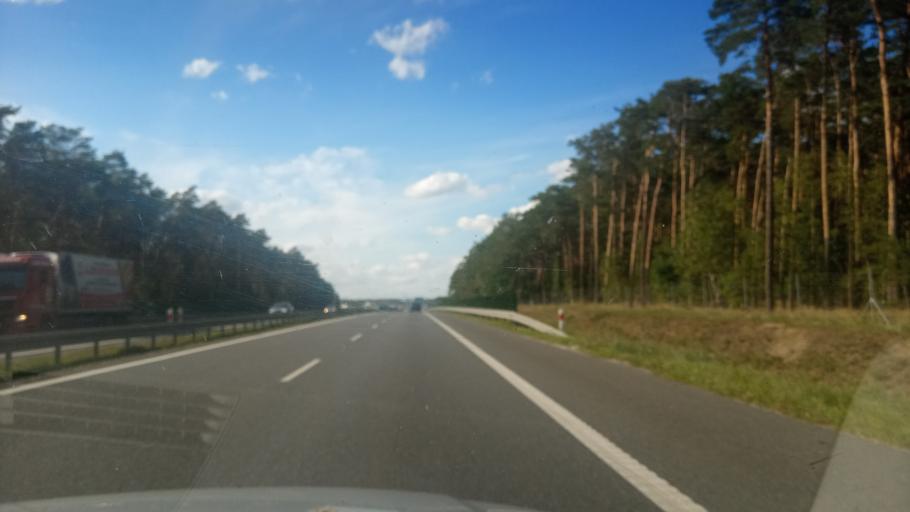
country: PL
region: Kujawsko-Pomorskie
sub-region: Powiat bydgoski
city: Biale Blota
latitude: 53.0815
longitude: 17.9094
